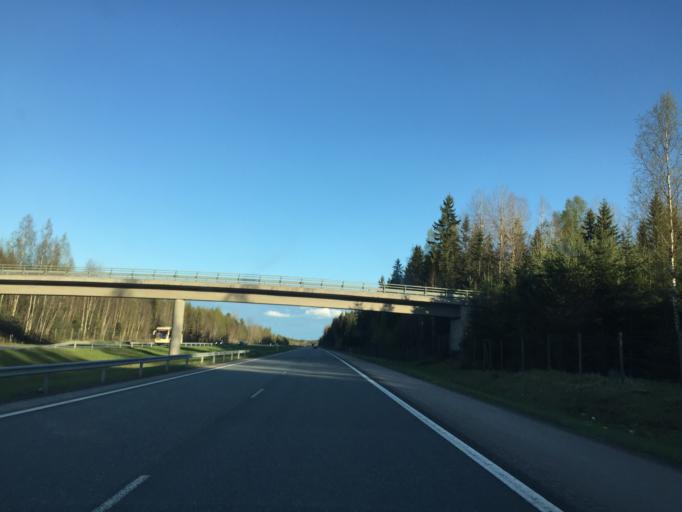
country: FI
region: Haeme
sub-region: Haemeenlinna
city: Tervakoski
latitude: 60.7953
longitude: 24.6900
